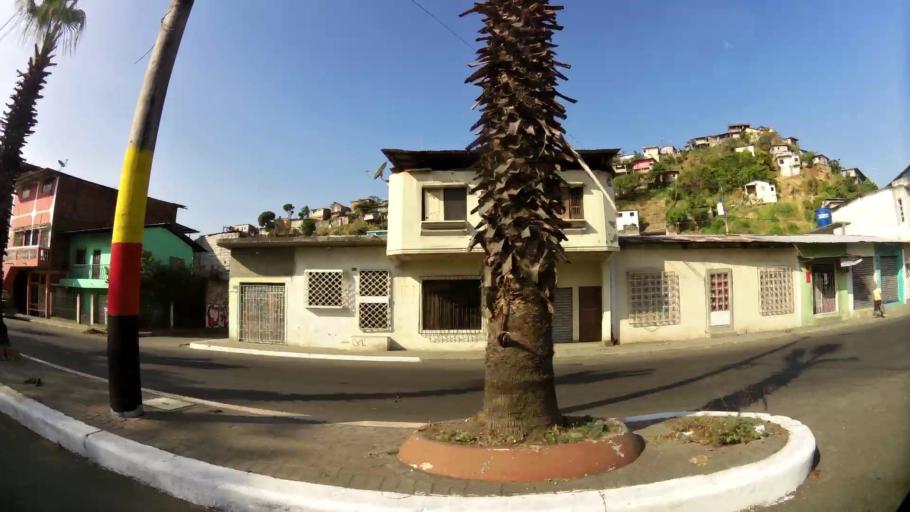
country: EC
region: Guayas
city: Eloy Alfaro
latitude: -2.1703
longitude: -79.8475
